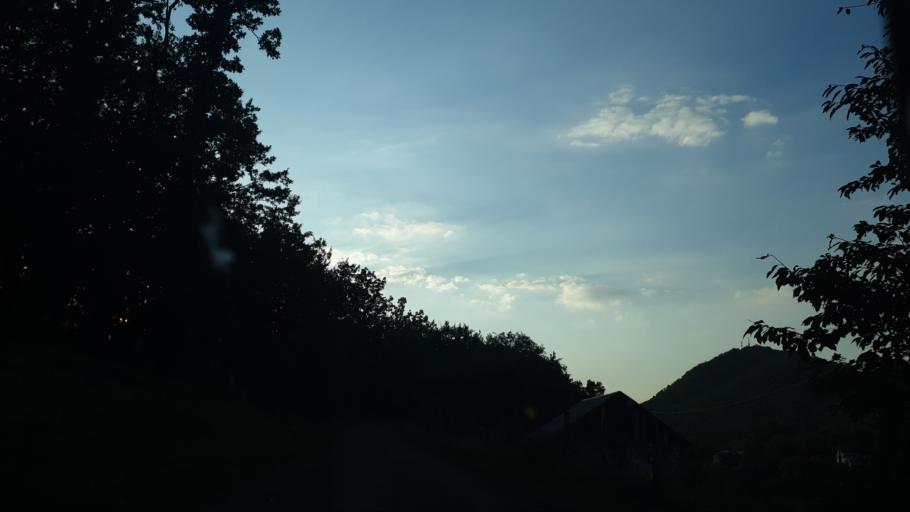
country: RS
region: Central Serbia
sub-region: Zlatiborski Okrug
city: Kosjeric
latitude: 44.0053
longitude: 19.9959
